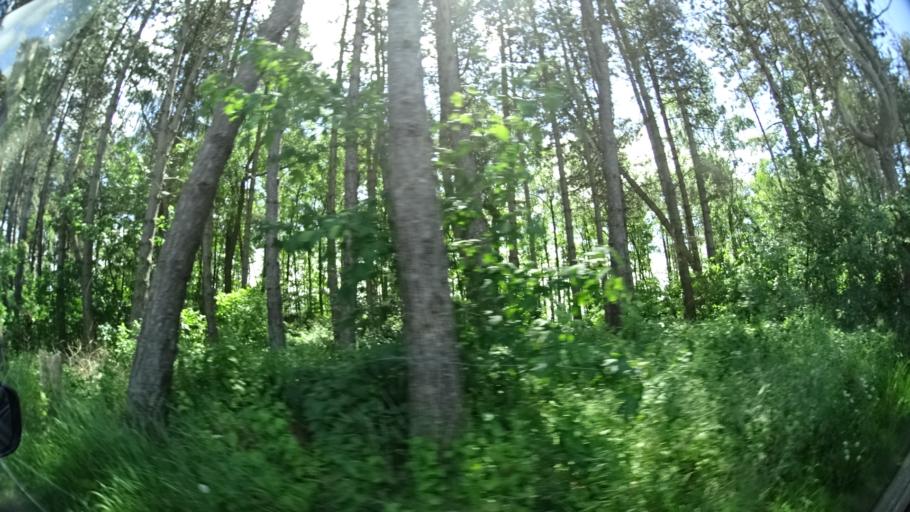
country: DK
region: Central Jutland
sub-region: Syddjurs Kommune
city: Ronde
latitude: 56.2942
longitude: 10.4233
